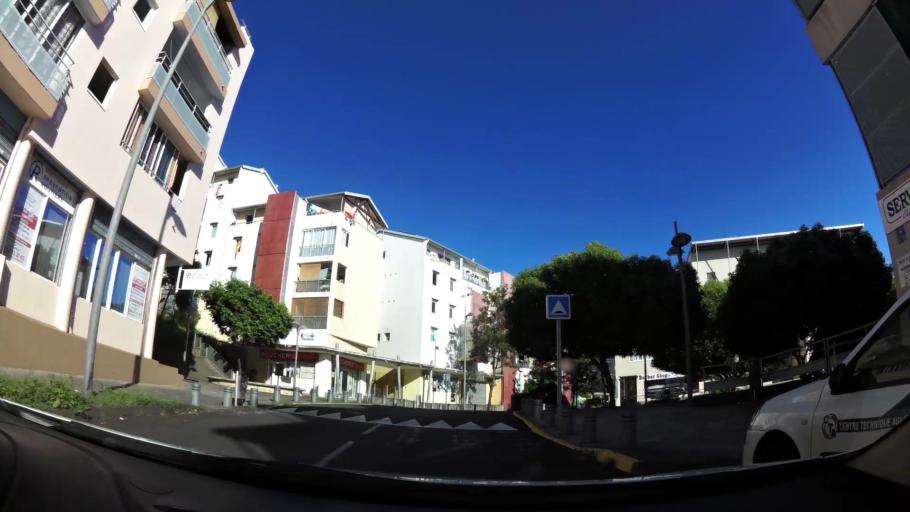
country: RE
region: Reunion
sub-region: Reunion
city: Saint-Denis
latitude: -20.8926
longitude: 55.4507
